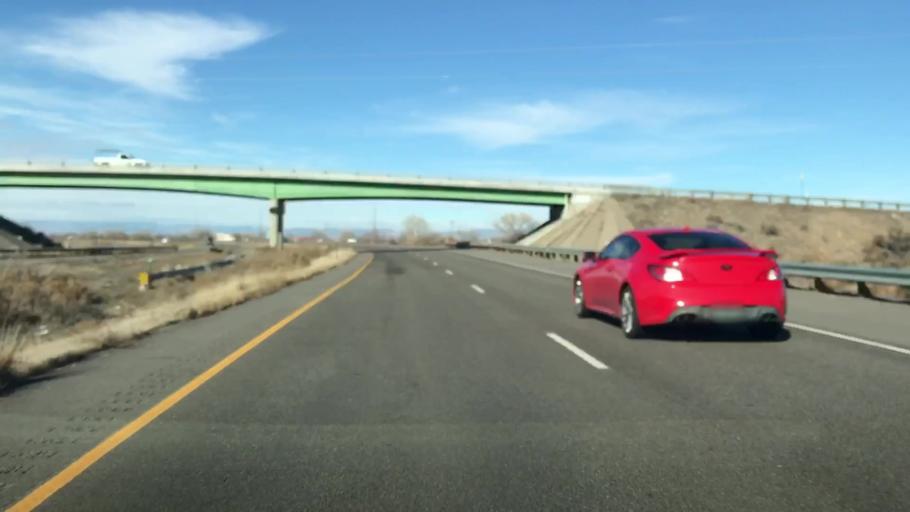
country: US
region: Colorado
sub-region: Mesa County
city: Fruita
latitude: 39.1275
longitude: -108.6833
